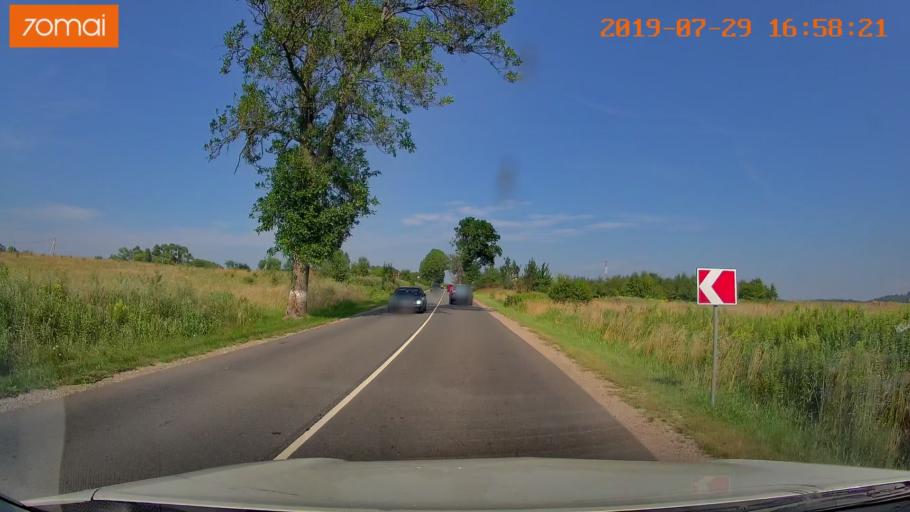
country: RU
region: Kaliningrad
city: Volochayevskoye
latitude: 54.8165
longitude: 20.2014
